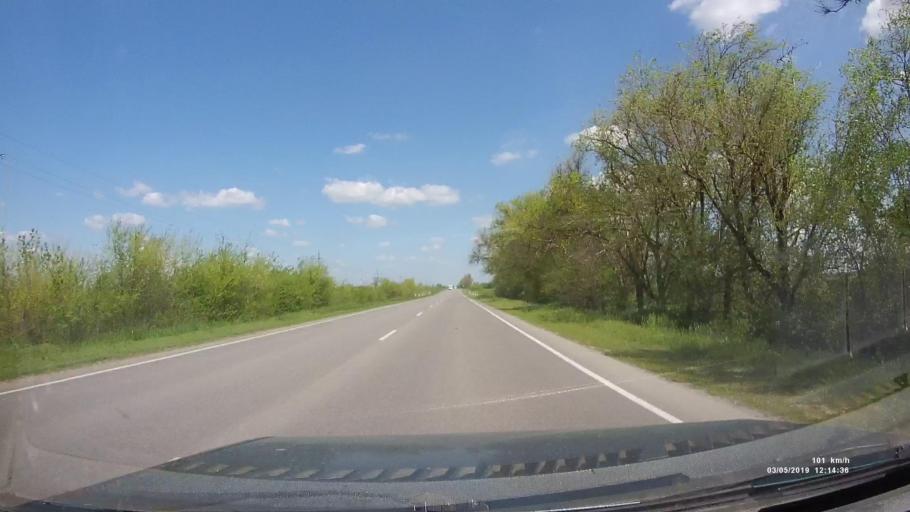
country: RU
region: Rostov
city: Melikhovskaya
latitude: 47.3463
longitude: 40.5651
